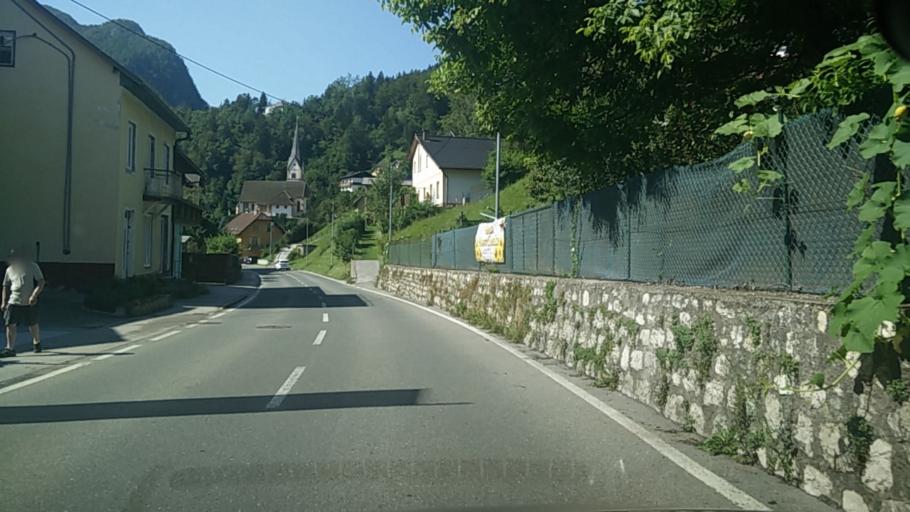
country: AT
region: Carinthia
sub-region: Politischer Bezirk Volkermarkt
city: Bad Eisenkappel
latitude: 46.4886
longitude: 14.5925
